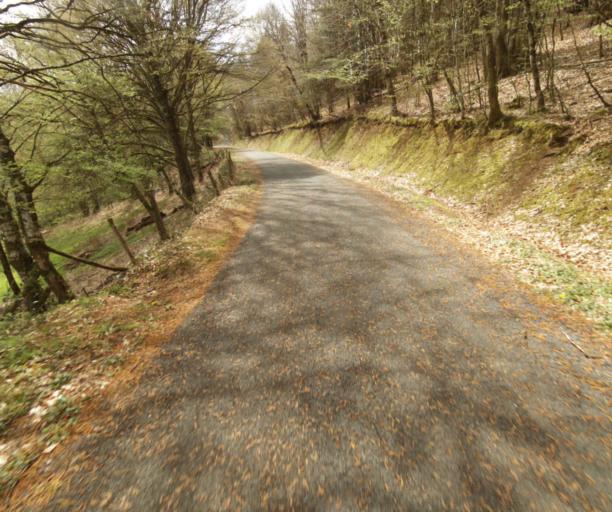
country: FR
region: Limousin
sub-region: Departement de la Correze
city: Laguenne
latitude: 45.2558
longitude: 1.8170
